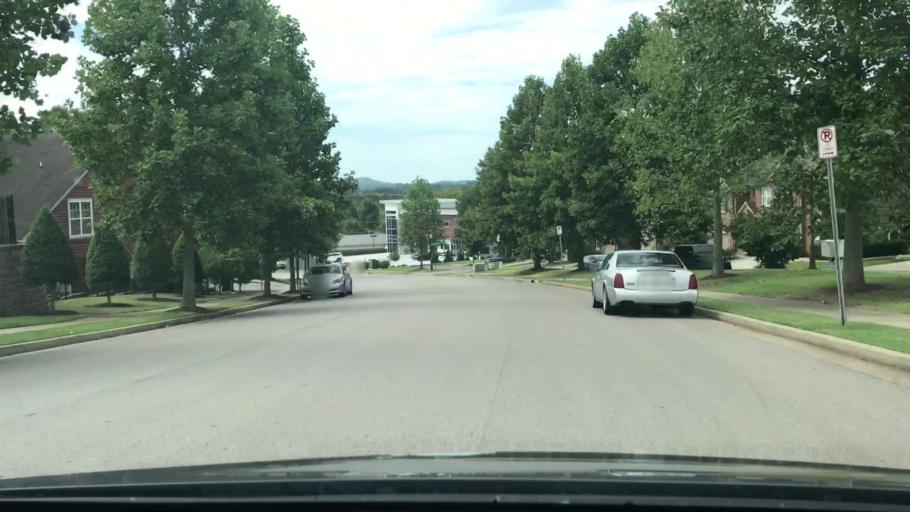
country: US
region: Tennessee
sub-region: Williamson County
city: Nolensville
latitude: 36.0019
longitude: -86.6926
